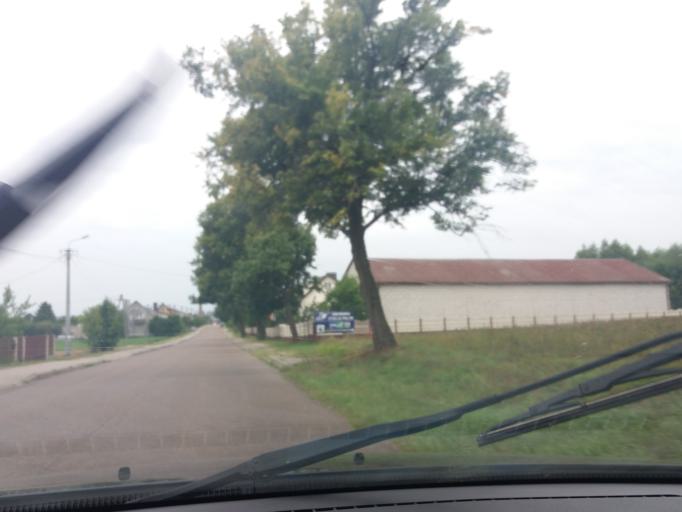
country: PL
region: Masovian Voivodeship
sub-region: Powiat mlawski
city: Wieczfnia Koscielna
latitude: 53.1988
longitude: 20.4859
